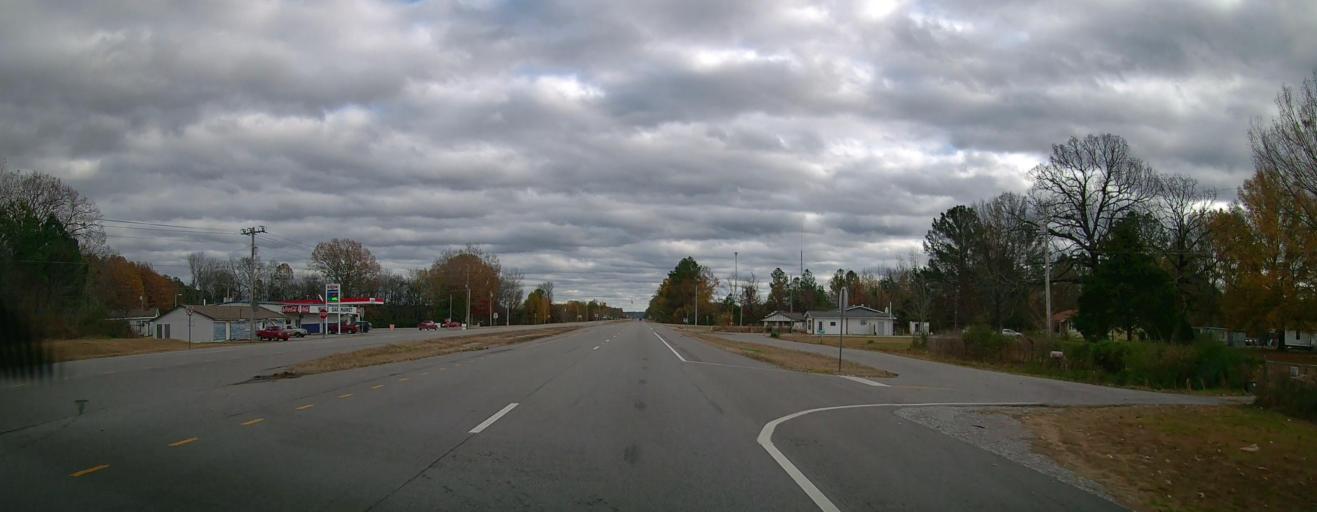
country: US
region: Alabama
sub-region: Lawrence County
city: Town Creek
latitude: 34.6546
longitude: -87.5309
